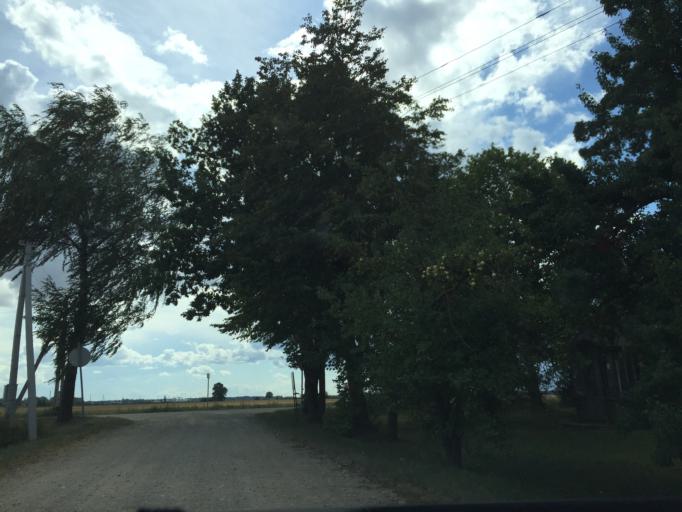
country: LT
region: Siauliu apskritis
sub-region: Joniskis
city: Joniskis
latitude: 56.3407
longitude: 23.6204
